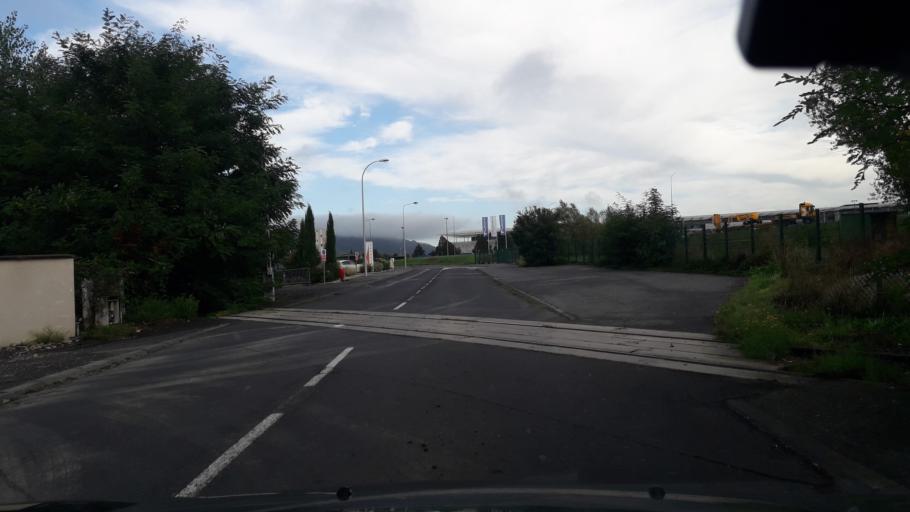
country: FR
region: Auvergne
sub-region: Departement du Puy-de-Dome
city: Gerzat
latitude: 45.8391
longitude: 3.1255
